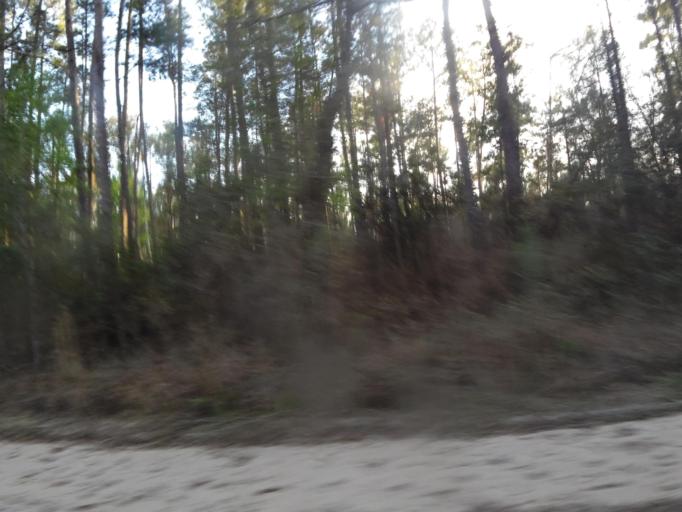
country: US
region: Florida
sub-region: Putnam County
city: Interlachen
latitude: 29.7809
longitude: -81.8591
